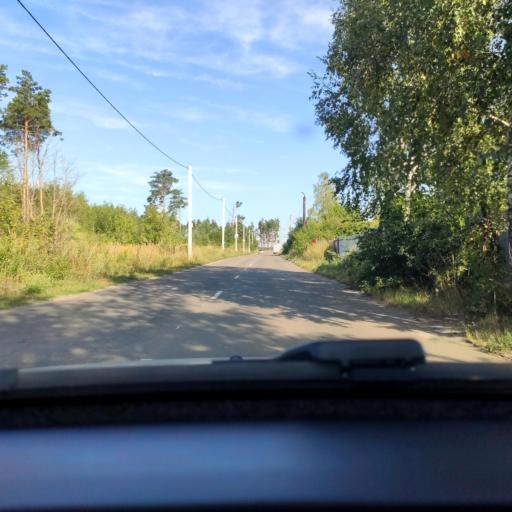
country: RU
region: Voronezj
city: Podgornoye
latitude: 51.8383
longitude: 39.1966
